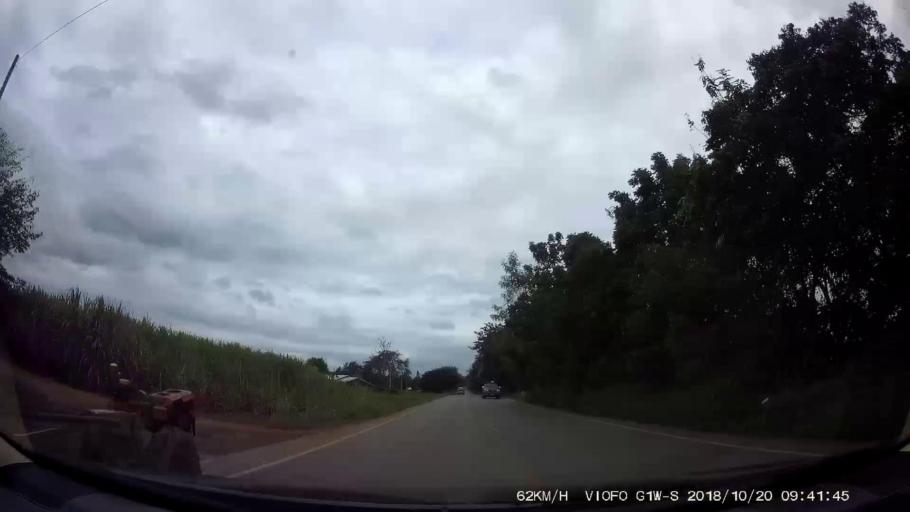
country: TH
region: Chaiyaphum
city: Khon San
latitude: 16.4564
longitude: 101.9556
